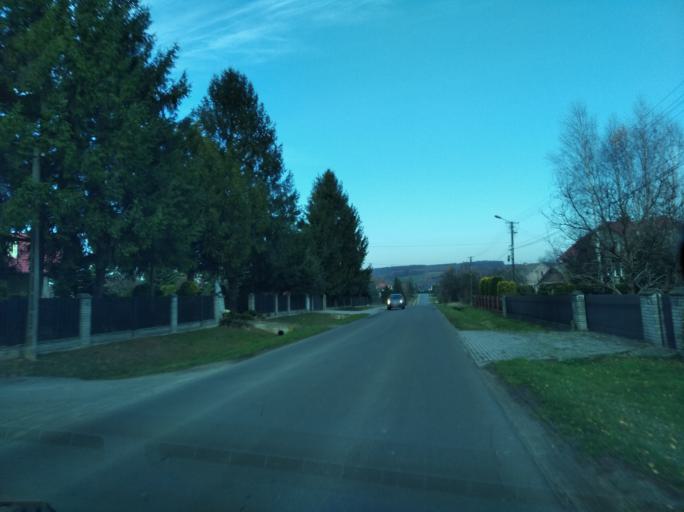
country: PL
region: Subcarpathian Voivodeship
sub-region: Powiat ropczycko-sedziszowski
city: Iwierzyce
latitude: 50.0224
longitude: 21.7537
